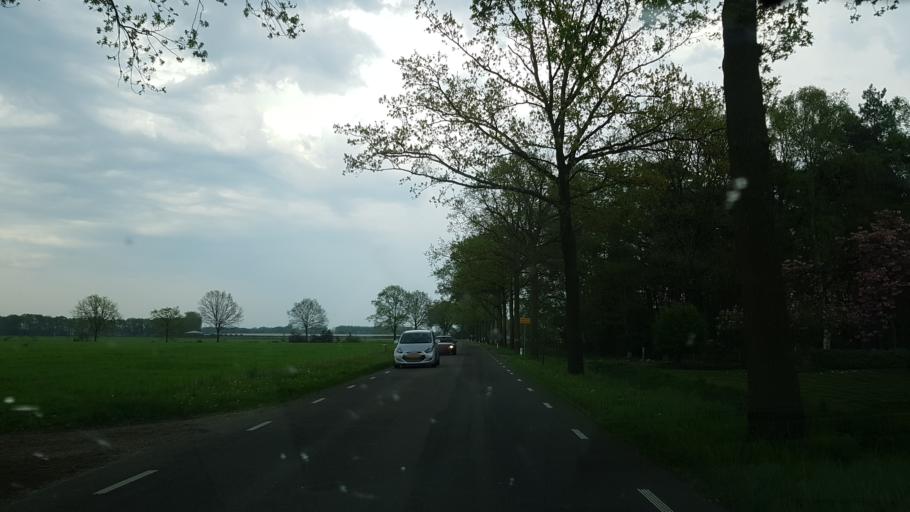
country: NL
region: Limburg
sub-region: Gemeente Nederweert
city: Nederweert
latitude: 51.3146
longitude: 5.7061
